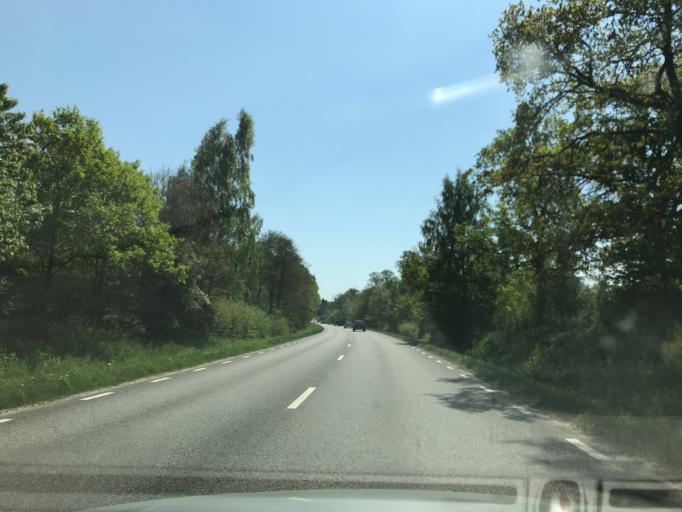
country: SE
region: Skane
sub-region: Angelholms Kommun
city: Munka-Ljungby
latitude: 56.2161
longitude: 13.0350
